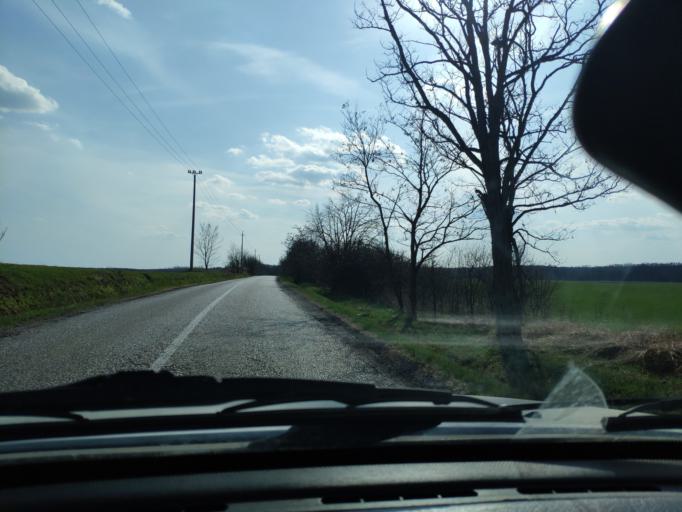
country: HU
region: Pest
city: Szigetujfalu
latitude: 47.2176
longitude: 18.9214
